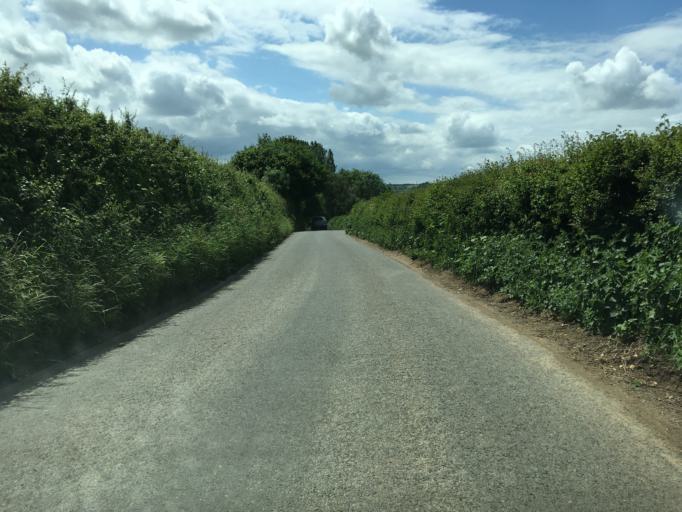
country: GB
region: England
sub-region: Gloucestershire
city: Stroud
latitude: 51.7539
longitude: -2.2194
